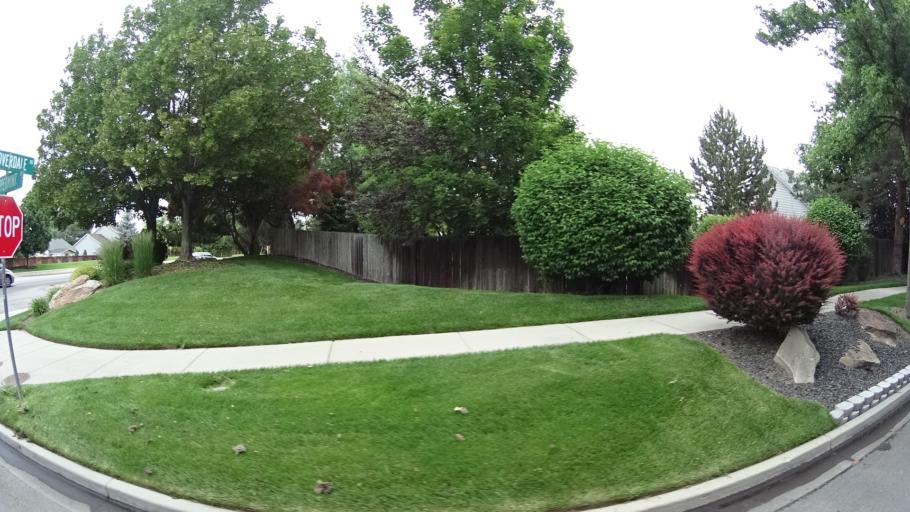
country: US
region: Idaho
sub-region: Ada County
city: Meridian
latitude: 43.5869
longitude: -116.3340
